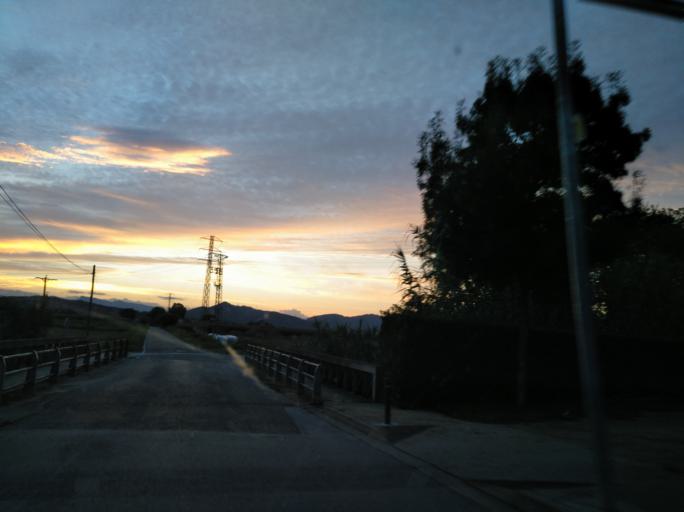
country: ES
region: Catalonia
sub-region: Provincia de Girona
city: Vilablareix
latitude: 41.9550
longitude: 2.7925
